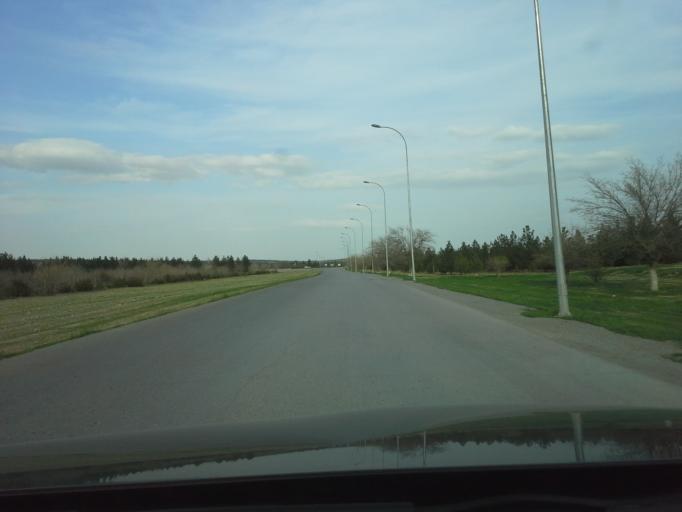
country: TM
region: Ahal
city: Abadan
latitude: 37.9353
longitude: 58.2318
